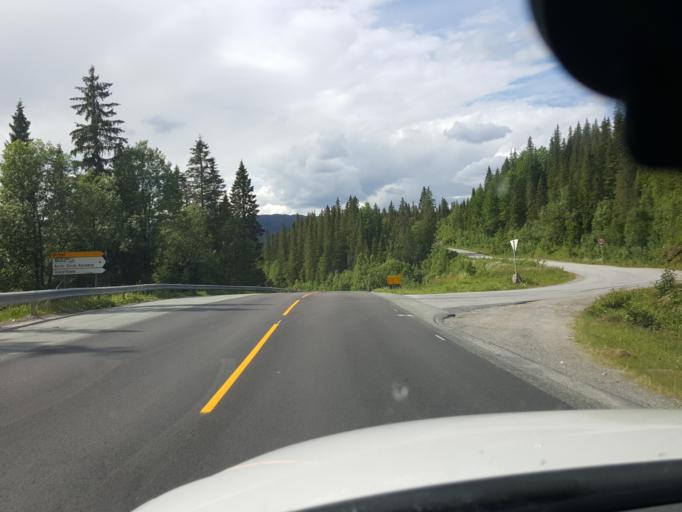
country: NO
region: Nordland
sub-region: Rana
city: Mo i Rana
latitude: 66.4076
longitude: 14.5177
